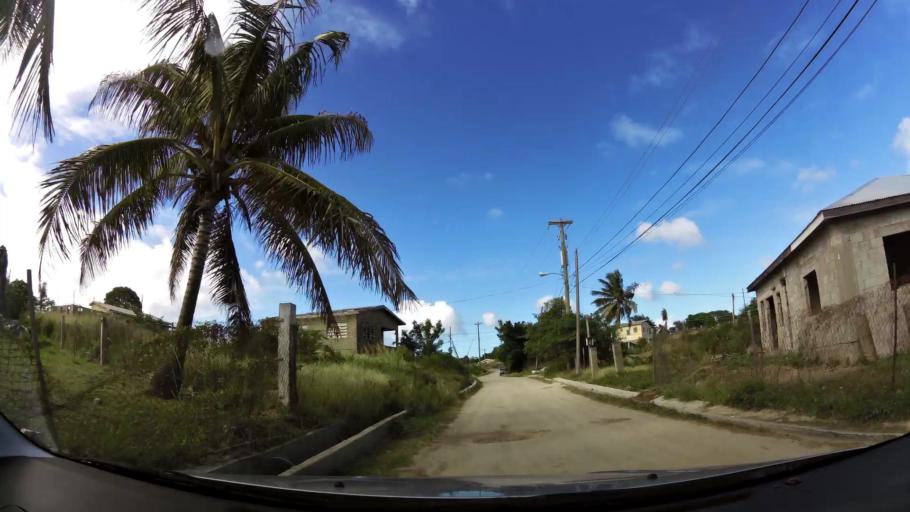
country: AG
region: Saint Peter
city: All Saints
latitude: 17.0480
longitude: -61.8002
